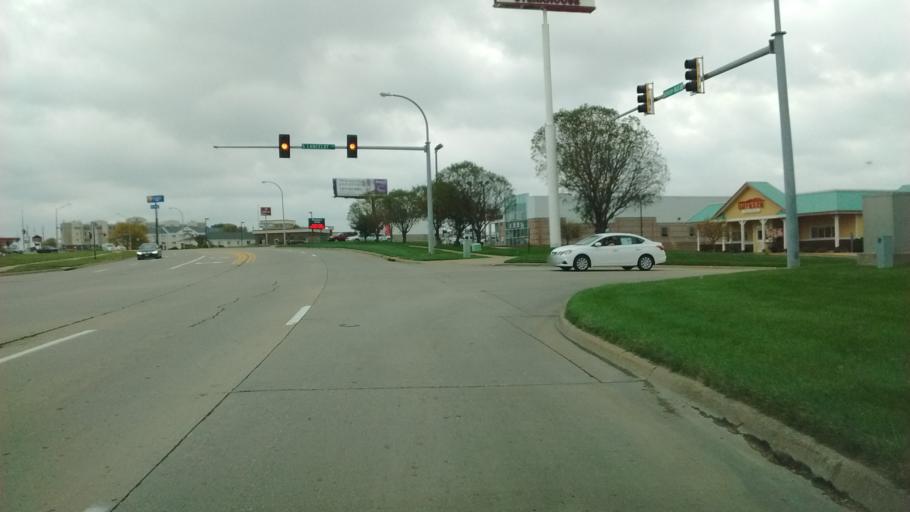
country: US
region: Iowa
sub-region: Woodbury County
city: Sergeant Bluff
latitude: 42.4408
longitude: -96.3508
